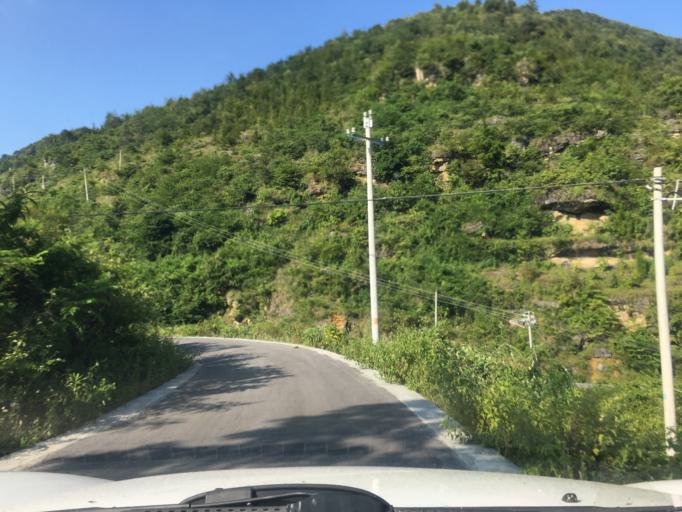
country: CN
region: Guangxi Zhuangzu Zizhiqu
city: Xinzhou
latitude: 25.4572
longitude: 105.7336
